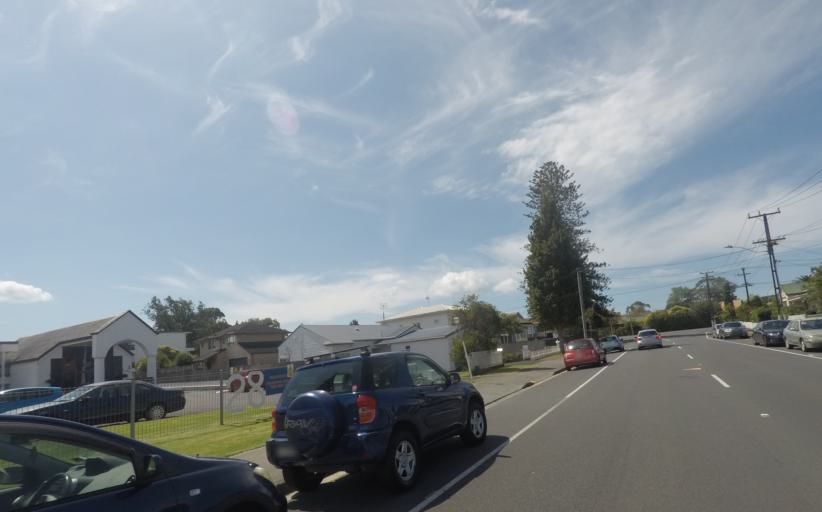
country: NZ
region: Auckland
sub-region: Auckland
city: Auckland
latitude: -36.8942
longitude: 174.8092
